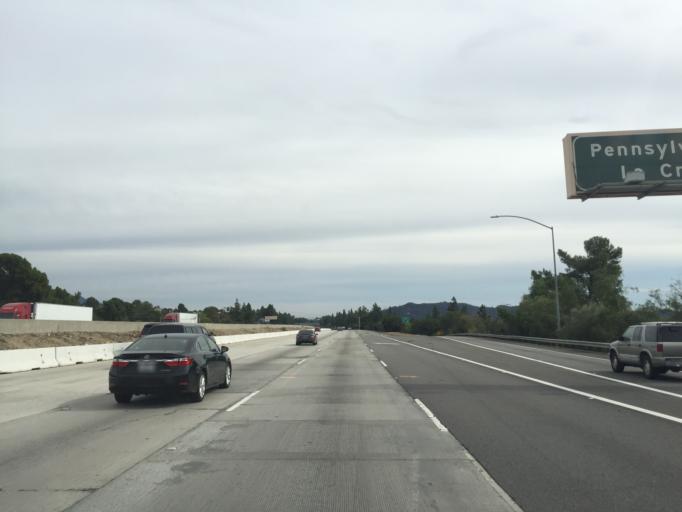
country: US
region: California
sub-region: Los Angeles County
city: La Crescenta-Montrose
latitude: 34.2253
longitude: -118.2527
